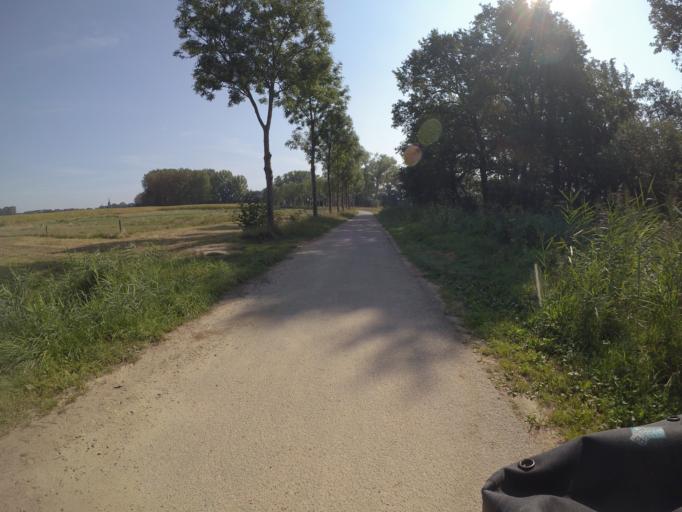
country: NL
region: North Brabant
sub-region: Gemeente Schijndel
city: Schijndel
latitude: 51.6492
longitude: 5.4517
